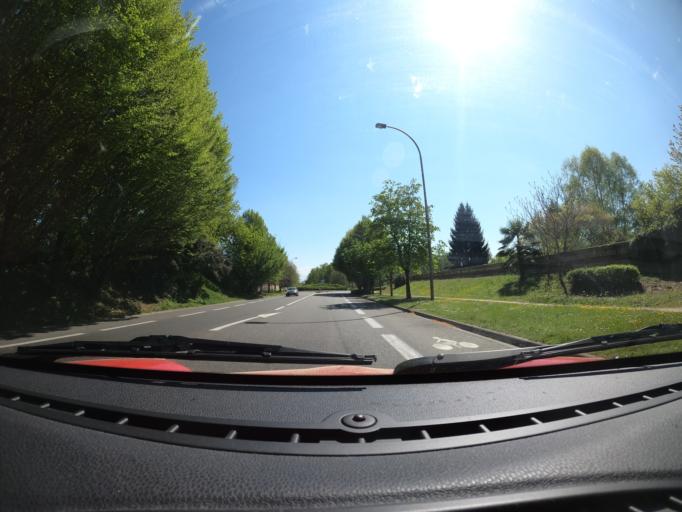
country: FR
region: Aquitaine
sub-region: Departement des Pyrenees-Atlantiques
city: Lons
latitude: 43.3368
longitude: -0.3851
